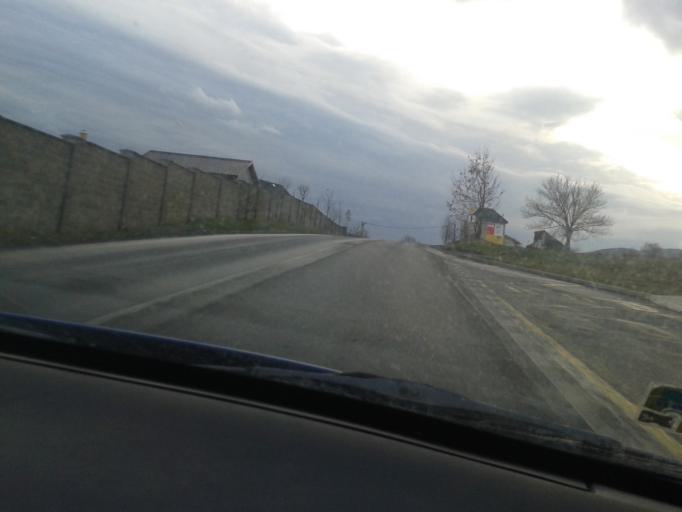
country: CZ
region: Central Bohemia
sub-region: Okres Beroun
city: Kraluv Dvur
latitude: 49.9340
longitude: 14.0099
